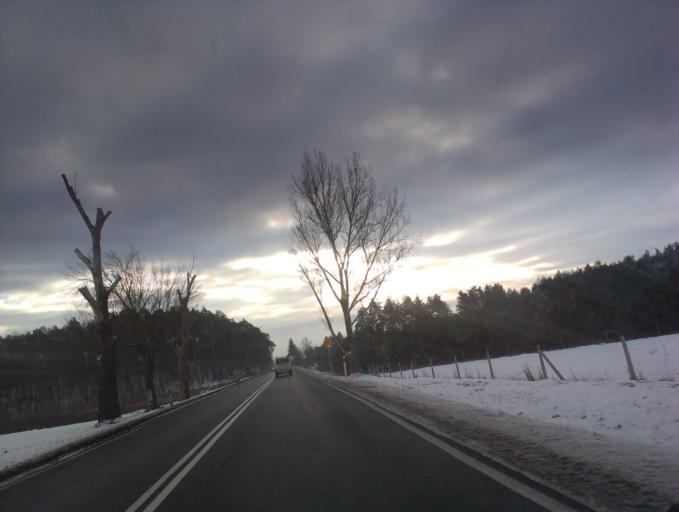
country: PL
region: Greater Poland Voivodeship
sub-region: Powiat zlotowski
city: Okonek
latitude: 53.5455
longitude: 16.8426
